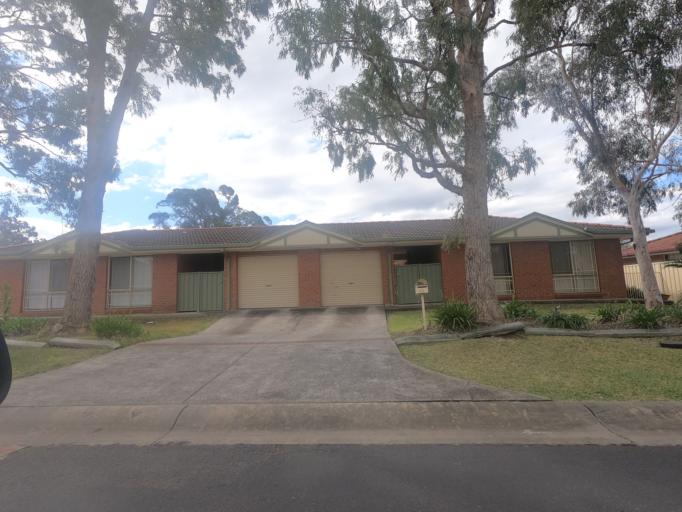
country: AU
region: New South Wales
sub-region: Wollongong
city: Dapto
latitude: -34.4898
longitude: 150.7749
